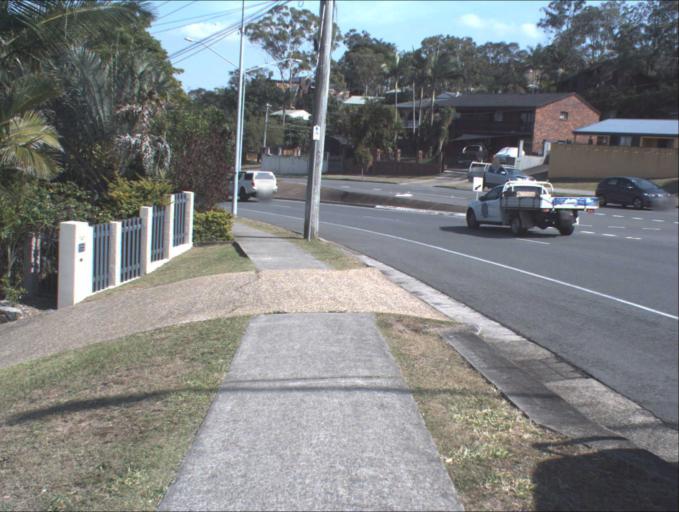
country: AU
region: Queensland
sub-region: Logan
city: Springwood
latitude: -27.6086
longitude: 153.1327
